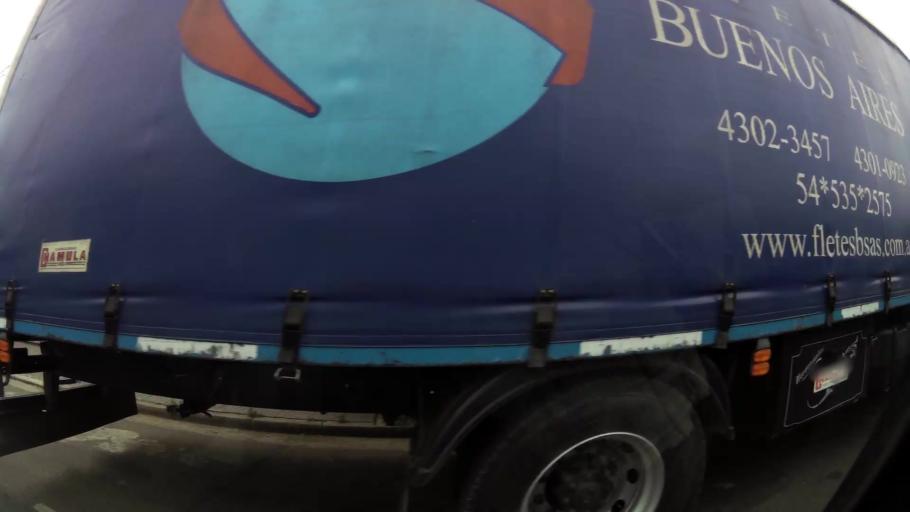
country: AR
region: Buenos Aires
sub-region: Partido de Avellaneda
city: Avellaneda
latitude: -34.6720
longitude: -58.3923
